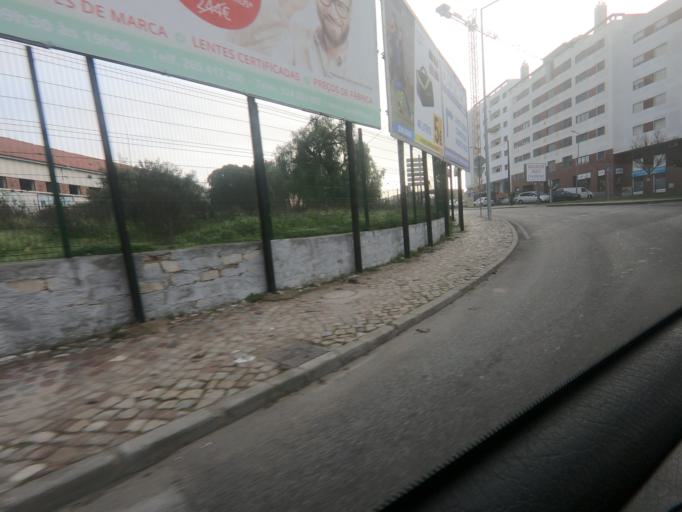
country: PT
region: Setubal
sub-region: Setubal
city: Setubal
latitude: 38.5322
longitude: -8.8753
